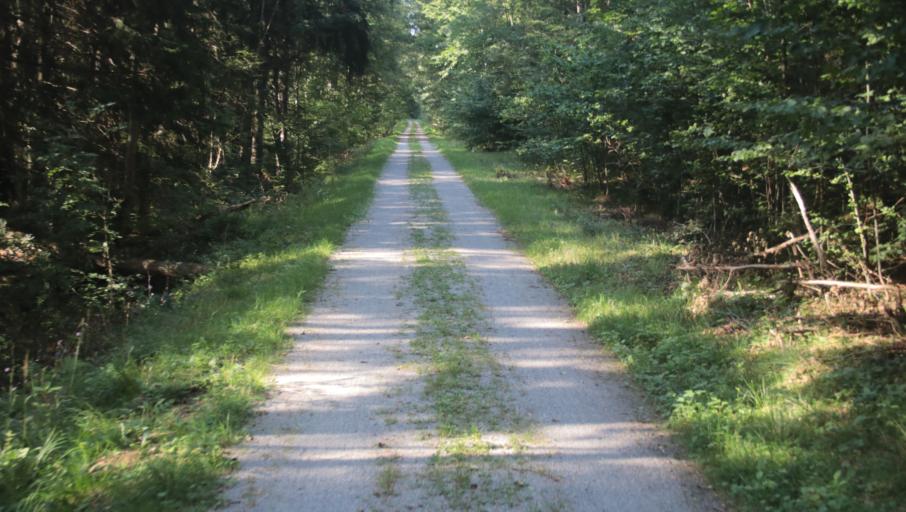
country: SE
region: Blekinge
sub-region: Karlshamns Kommun
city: Svangsta
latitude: 56.3662
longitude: 14.6862
